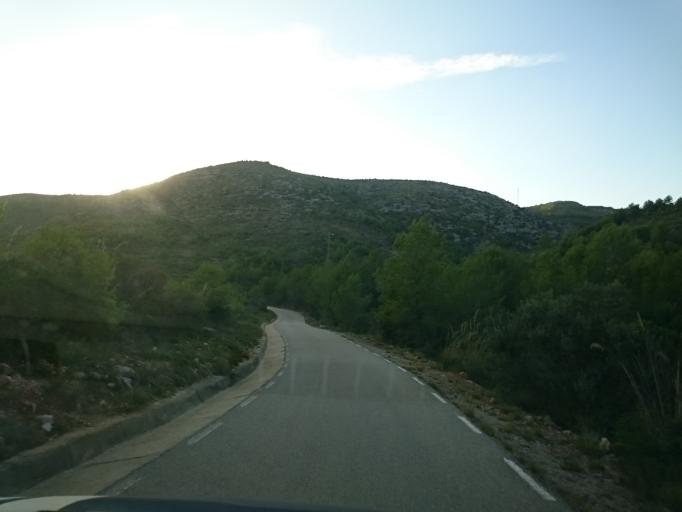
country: ES
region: Catalonia
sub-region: Provincia de Barcelona
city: Olivella
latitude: 41.3021
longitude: 1.8486
